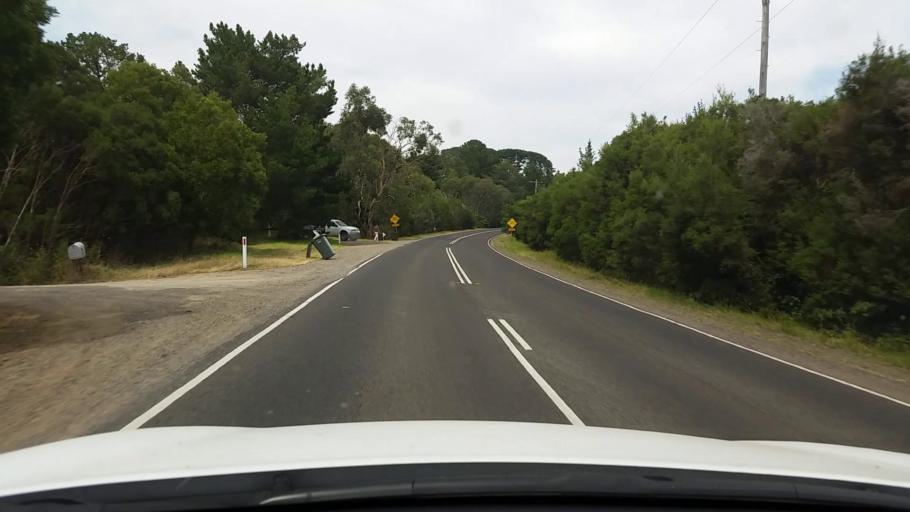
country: AU
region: Victoria
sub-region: Mornington Peninsula
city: Merricks
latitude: -38.3973
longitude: 145.0835
